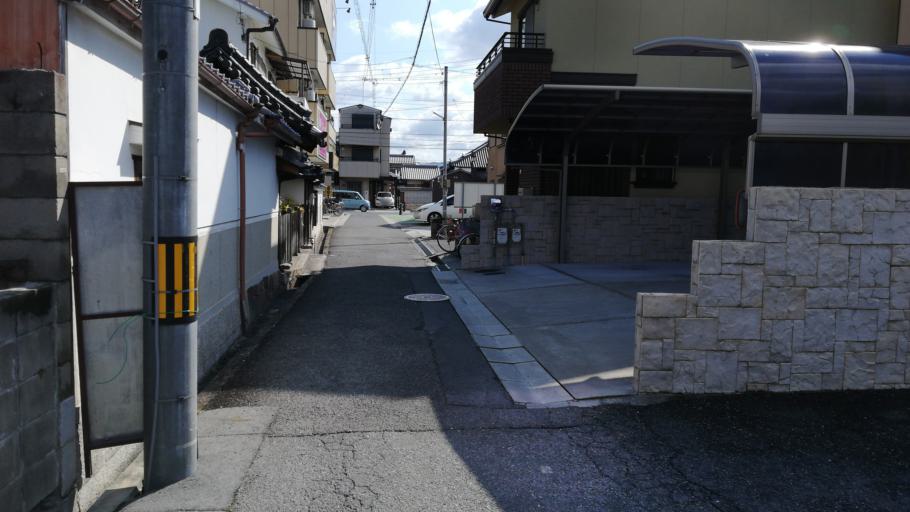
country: JP
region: Nara
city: Nara-shi
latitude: 34.6473
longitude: 135.7850
